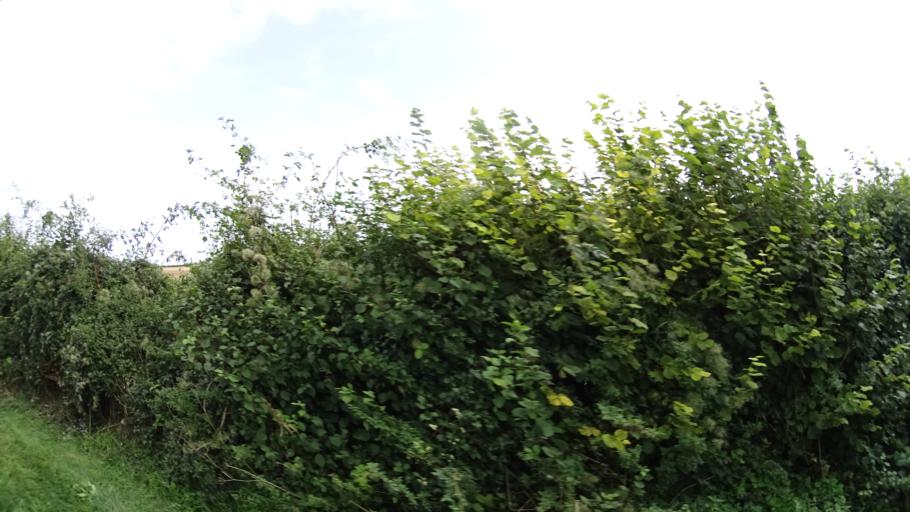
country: GB
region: England
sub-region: Wiltshire
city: Bower Chalke
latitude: 50.8979
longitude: -2.0324
